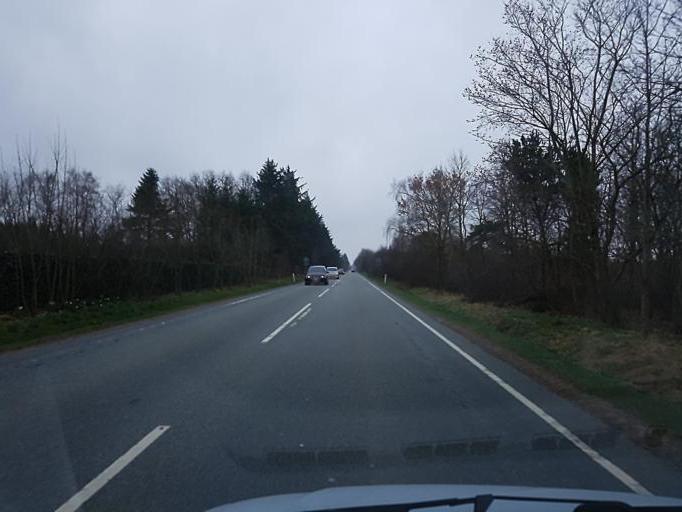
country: DK
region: Central Jutland
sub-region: Ringkobing-Skjern Kommune
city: Tarm
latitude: 55.8872
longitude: 8.5106
